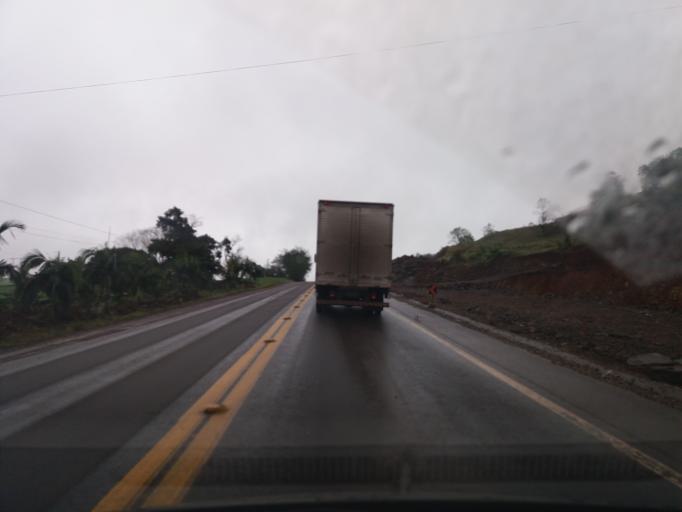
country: BR
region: Parana
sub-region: Realeza
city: Realeza
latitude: -25.4241
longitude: -53.5752
